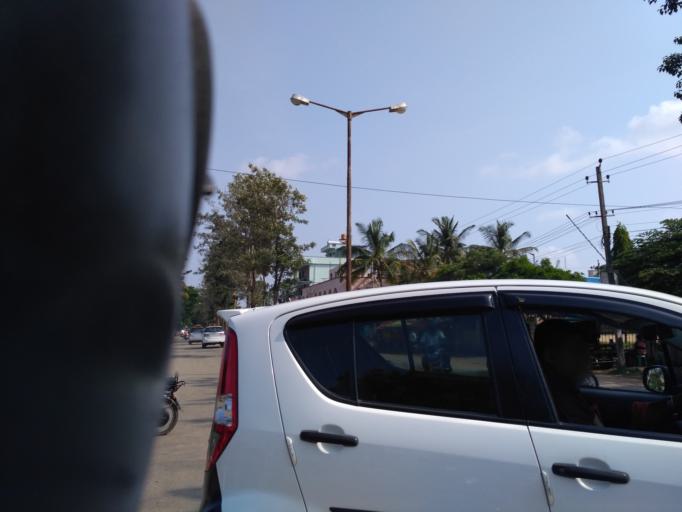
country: IN
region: Karnataka
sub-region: Hassan
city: Hassan
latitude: 13.0172
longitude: 76.1056
